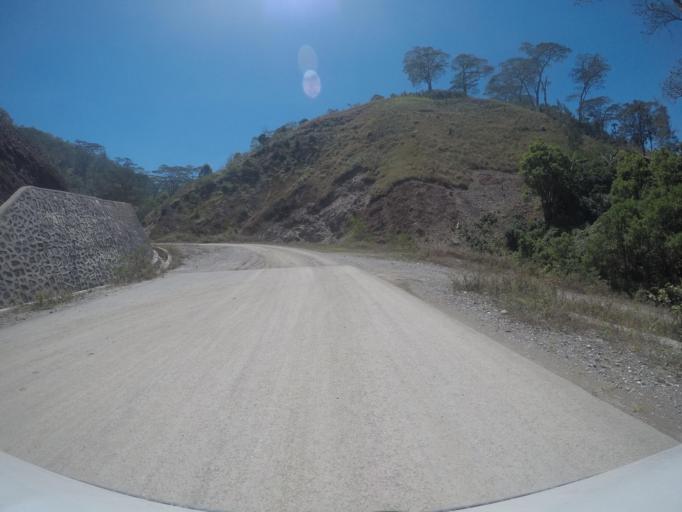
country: TL
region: Ermera
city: Gleno
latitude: -8.7783
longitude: 125.3834
